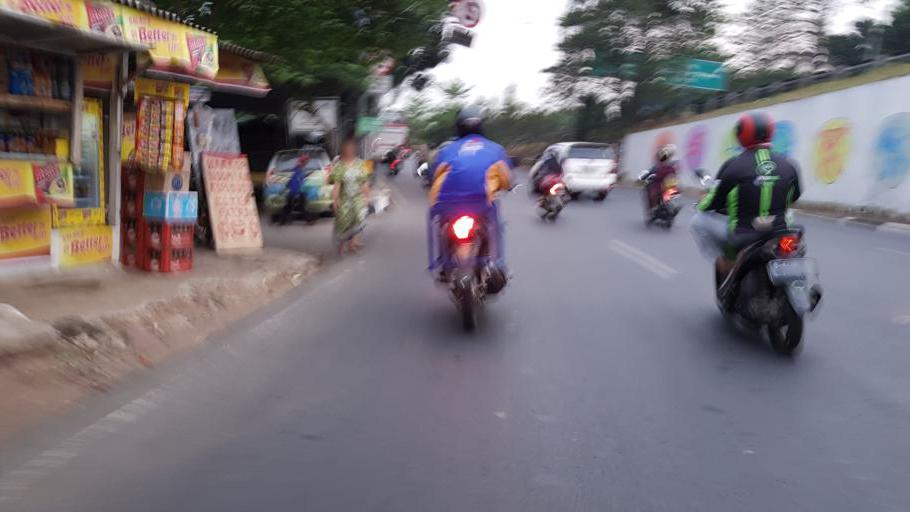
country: ID
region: Jakarta Raya
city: Jakarta
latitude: -6.3063
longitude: 106.8871
